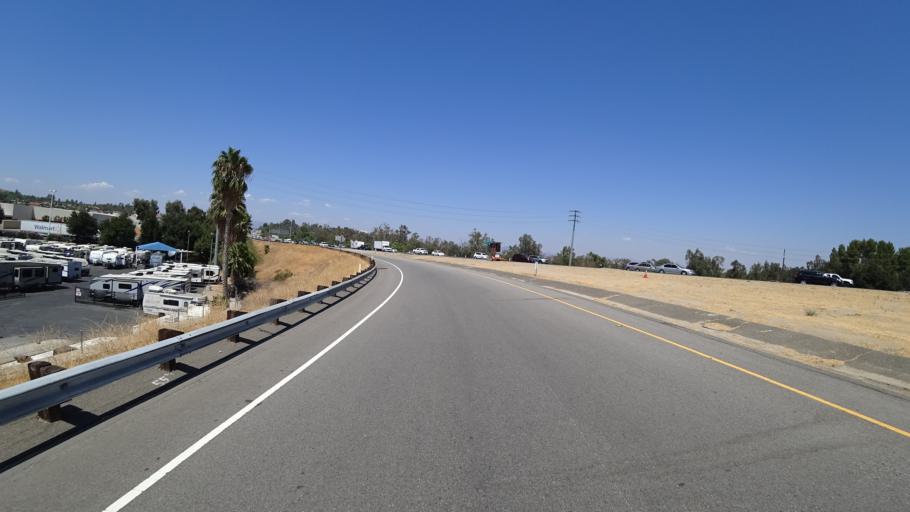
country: US
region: California
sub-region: Los Angeles County
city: Santa Clarita
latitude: 34.3816
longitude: -118.5678
